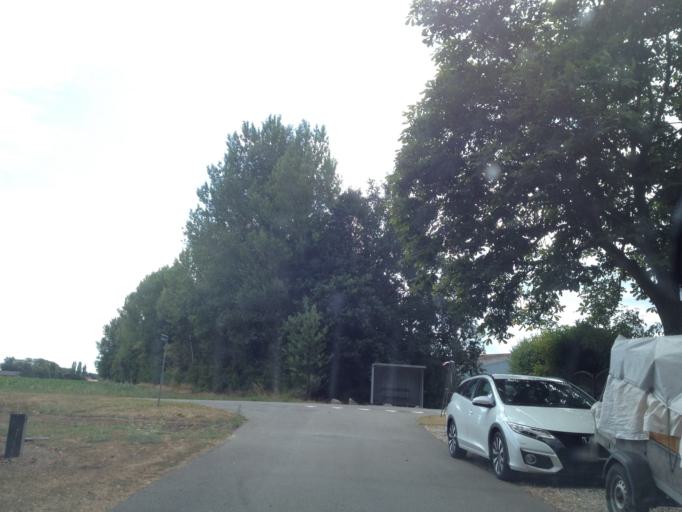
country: DK
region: Zealand
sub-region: Guldborgsund Kommune
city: Sakskobing
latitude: 54.7622
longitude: 11.6622
